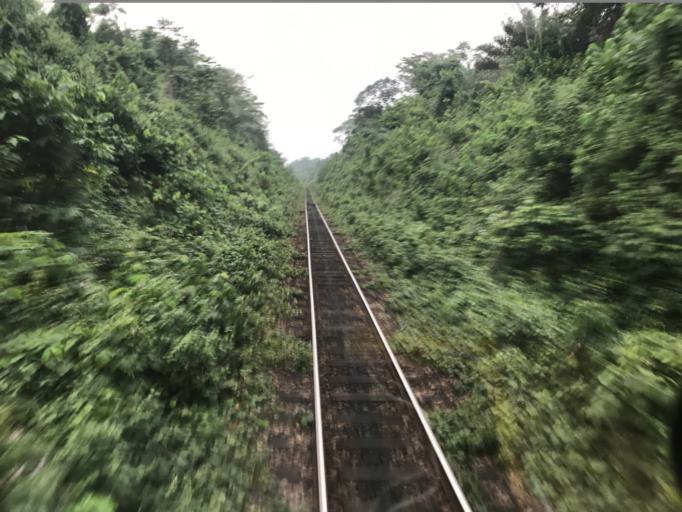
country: CM
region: Littoral
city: Edea
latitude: 3.9282
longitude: 10.1076
